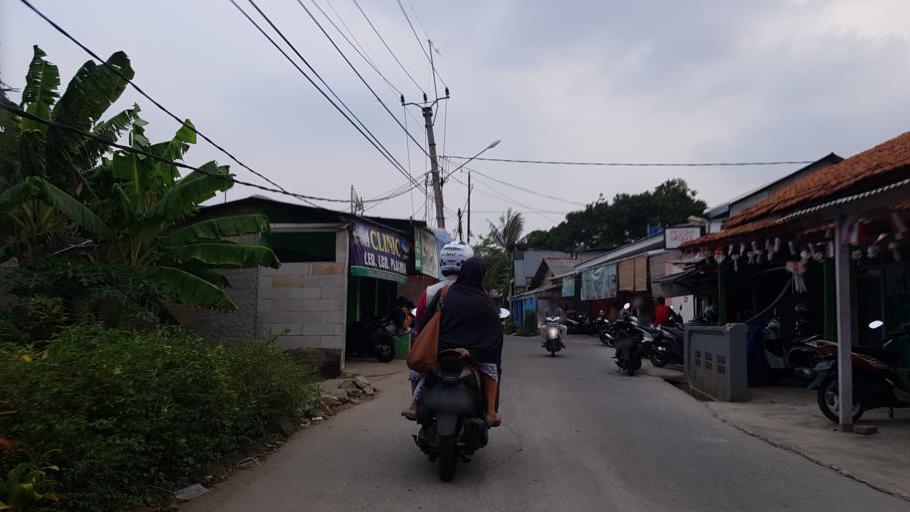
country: ID
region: West Java
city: Sawangan
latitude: -6.3785
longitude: 106.7947
